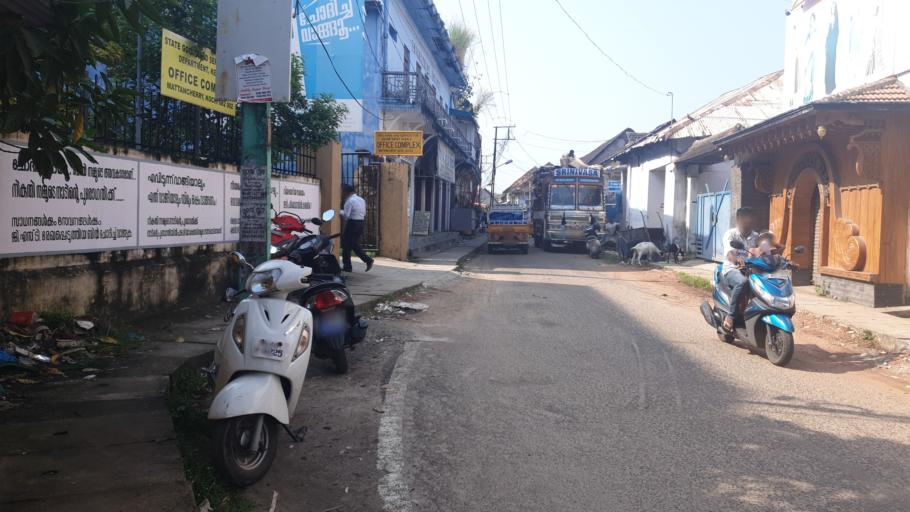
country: IN
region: Kerala
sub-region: Ernakulam
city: Cochin
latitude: 9.9624
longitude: 76.2575
